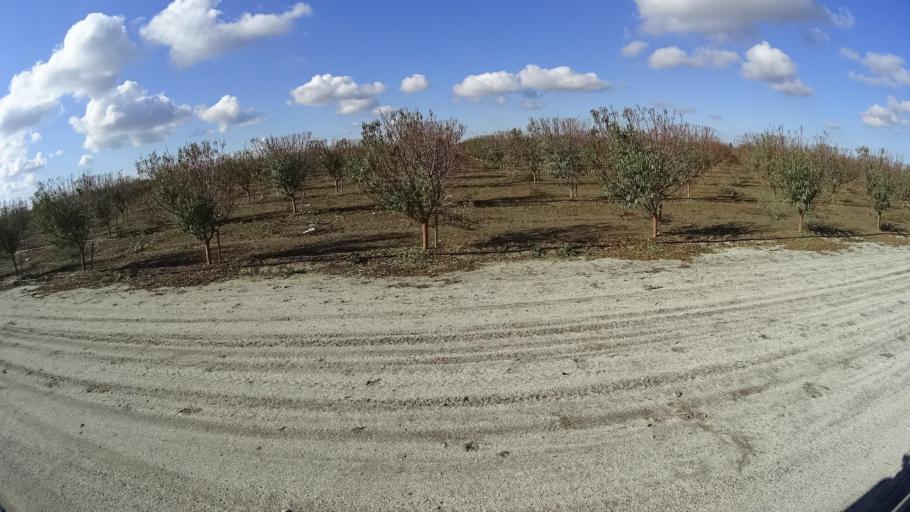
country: US
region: California
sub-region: Kern County
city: McFarland
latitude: 35.6574
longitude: -119.2322
